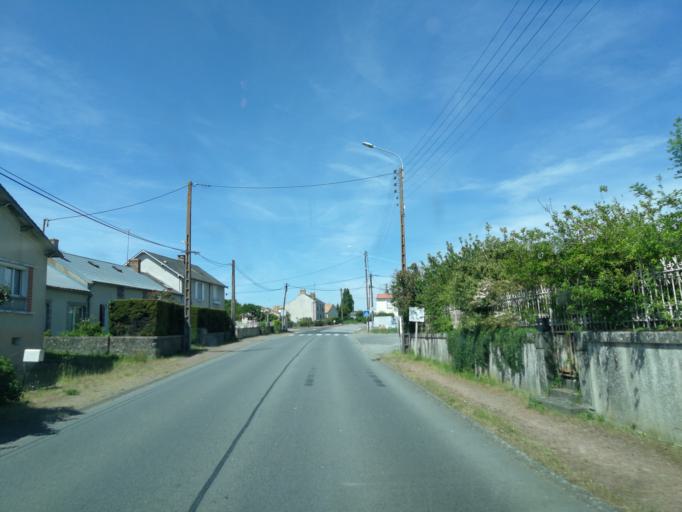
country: FR
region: Poitou-Charentes
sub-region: Departement des Deux-Sevres
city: Saint-Varent
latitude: 46.9015
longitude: -0.2879
